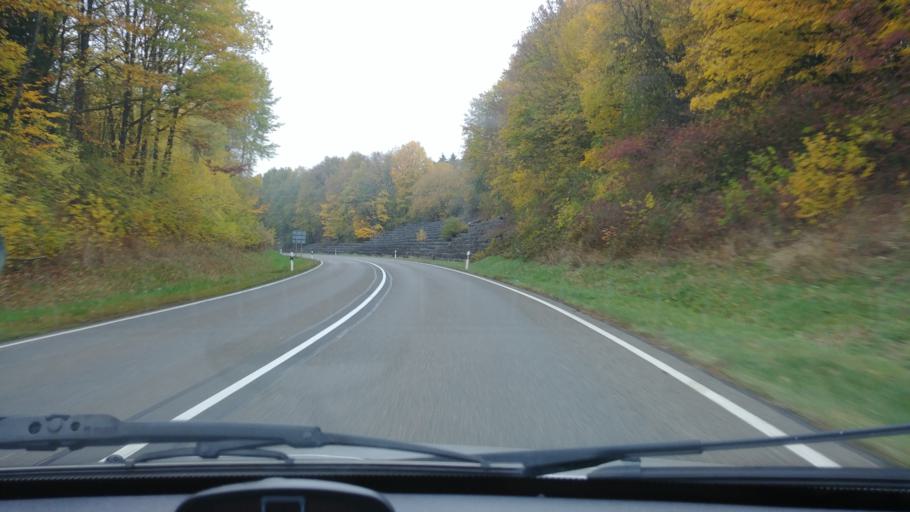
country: DE
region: Rheinland-Pfalz
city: Langenhahn
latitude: 50.5833
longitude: 7.9273
